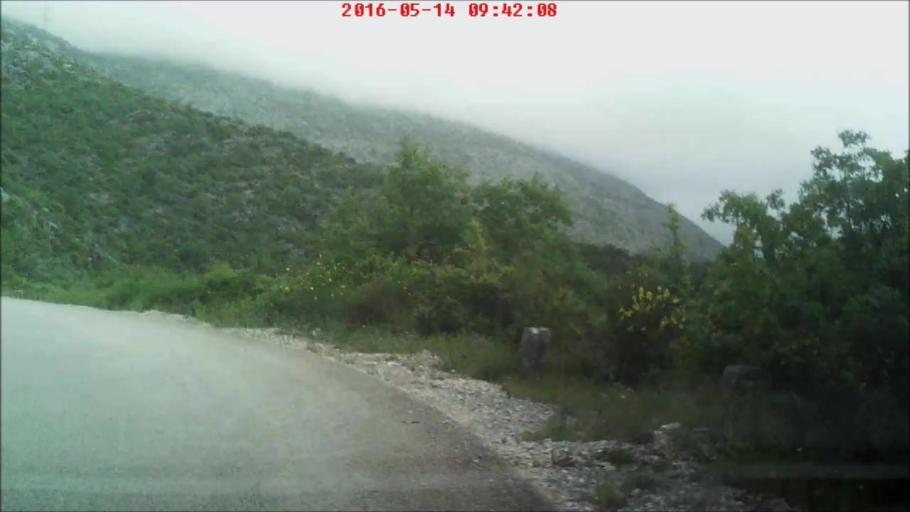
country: HR
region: Dubrovacko-Neretvanska
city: Podgora
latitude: 42.7887
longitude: 17.9006
